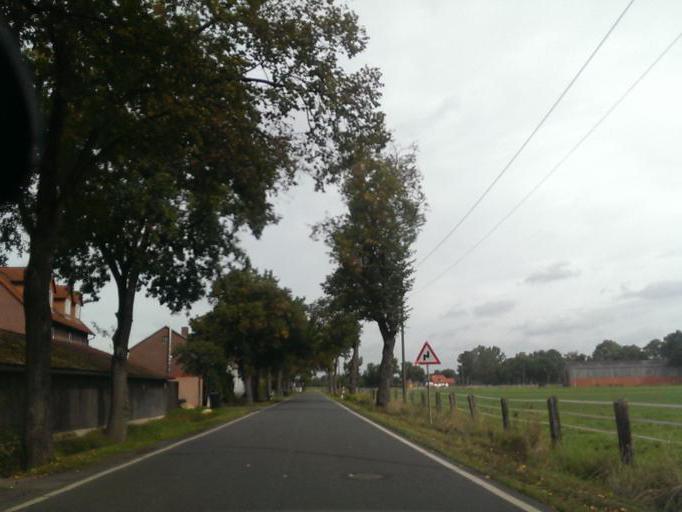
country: DE
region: Lower Saxony
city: Garbsen-Mitte
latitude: 52.4698
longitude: 9.6187
